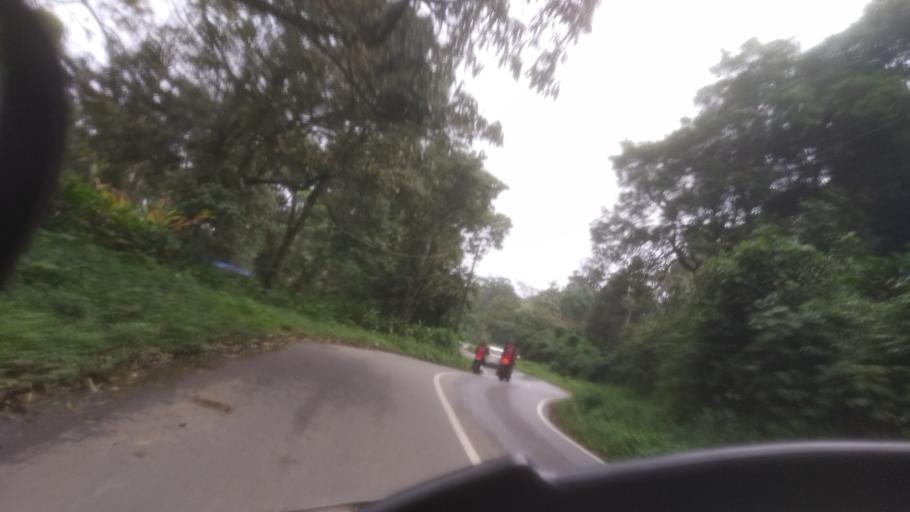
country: IN
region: Tamil Nadu
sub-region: Theni
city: Kombai
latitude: 9.8928
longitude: 77.1996
